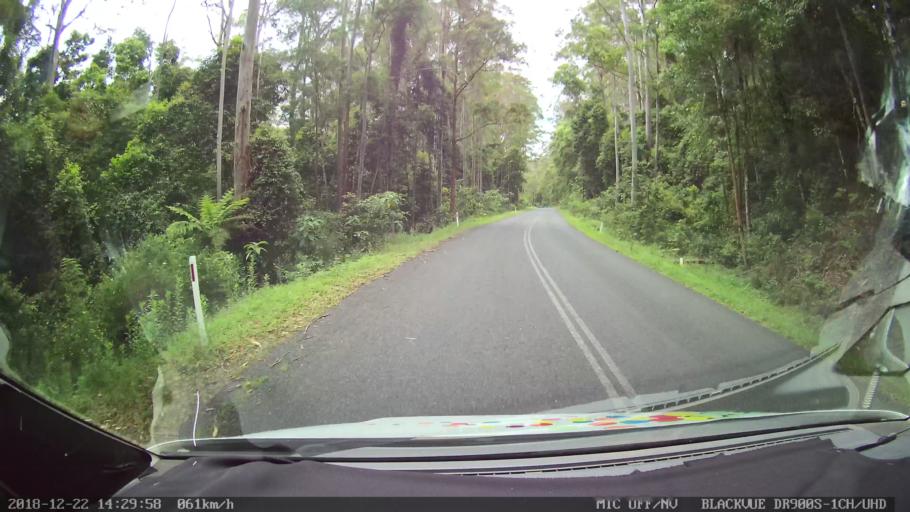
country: AU
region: New South Wales
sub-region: Bellingen
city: Dorrigo
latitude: -30.0815
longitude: 152.6338
